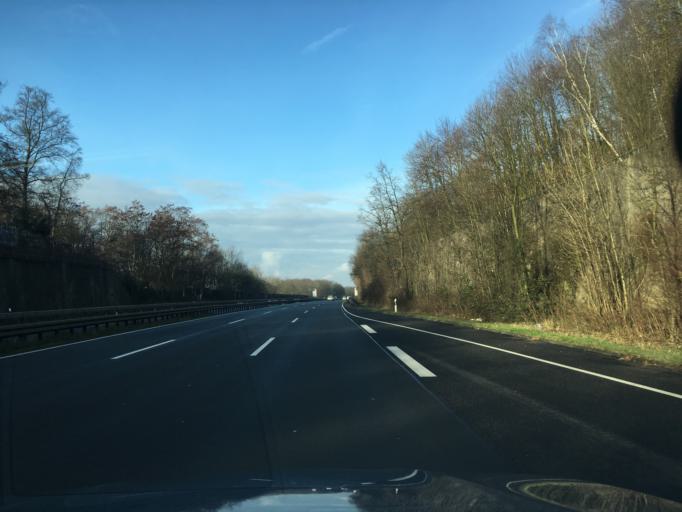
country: DE
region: North Rhine-Westphalia
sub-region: Regierungsbezirk Koln
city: Konigswinter
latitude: 50.7305
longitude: 7.1542
